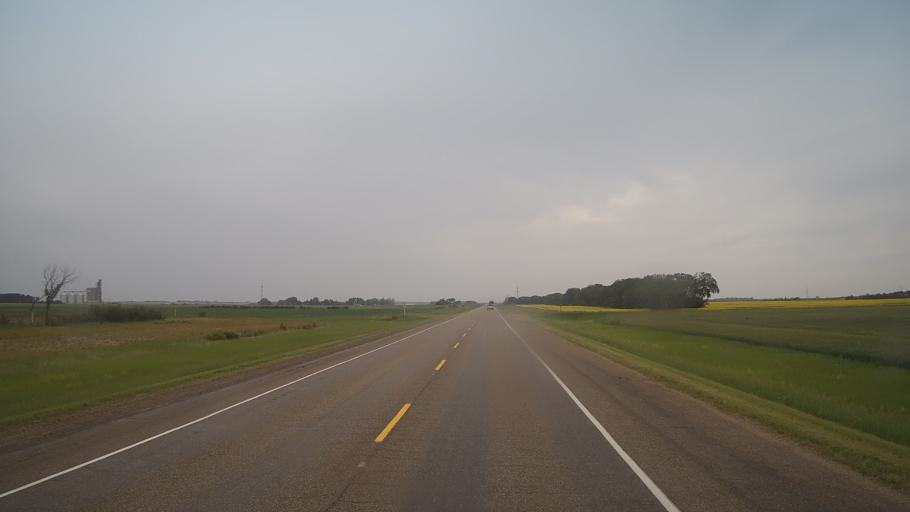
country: CA
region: Saskatchewan
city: Saskatoon
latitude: 52.1292
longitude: -106.8342
